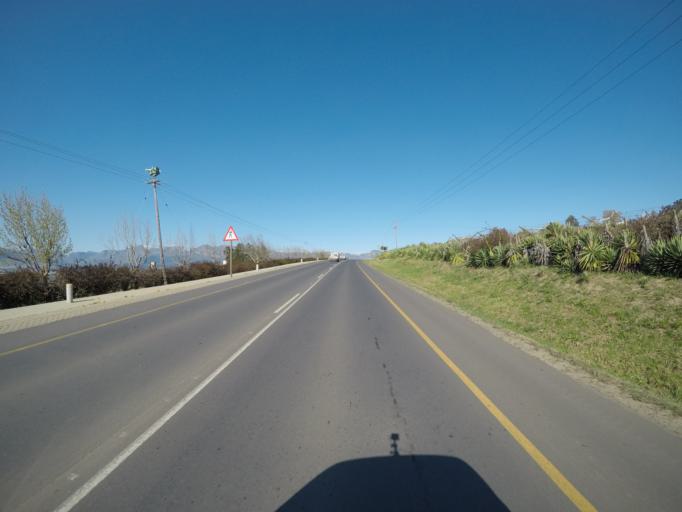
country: ZA
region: Western Cape
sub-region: Cape Winelands District Municipality
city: Noorder-Paarl
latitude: -33.6779
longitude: 18.9400
